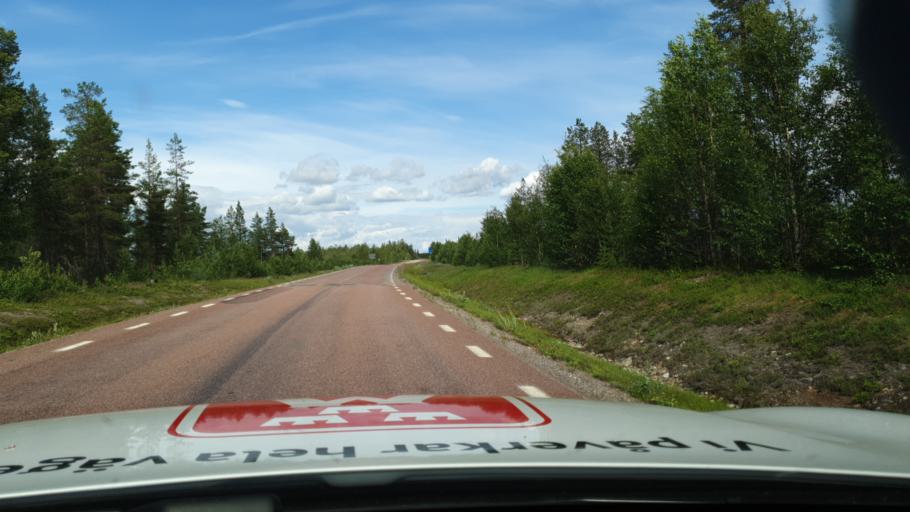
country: SE
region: Dalarna
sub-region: Alvdalens Kommun
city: AElvdalen
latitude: 61.7586
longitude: 13.4561
